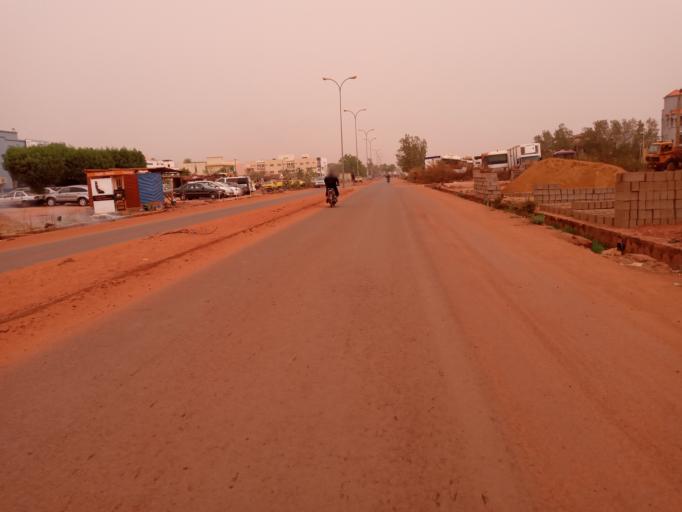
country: ML
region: Bamako
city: Bamako
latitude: 12.6508
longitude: -7.9334
